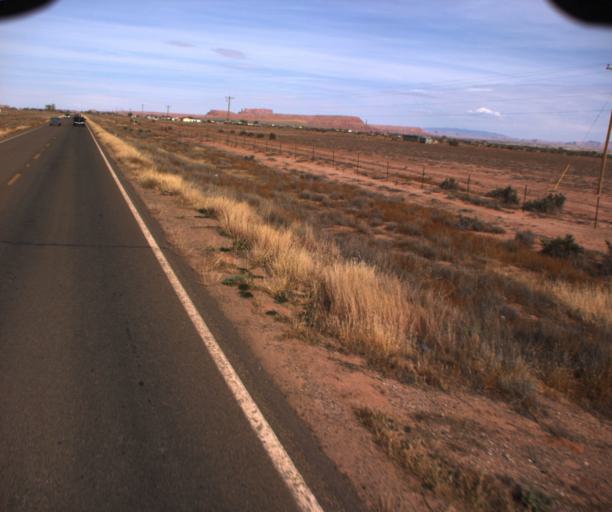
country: US
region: Arizona
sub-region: Apache County
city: Many Farms
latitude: 36.3893
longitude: -109.6105
